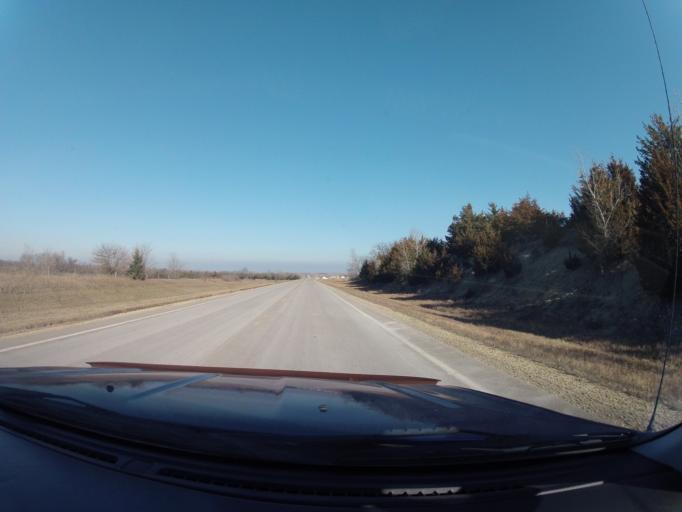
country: US
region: Kansas
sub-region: Marshall County
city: Blue Rapids
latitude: 39.4221
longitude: -96.7644
